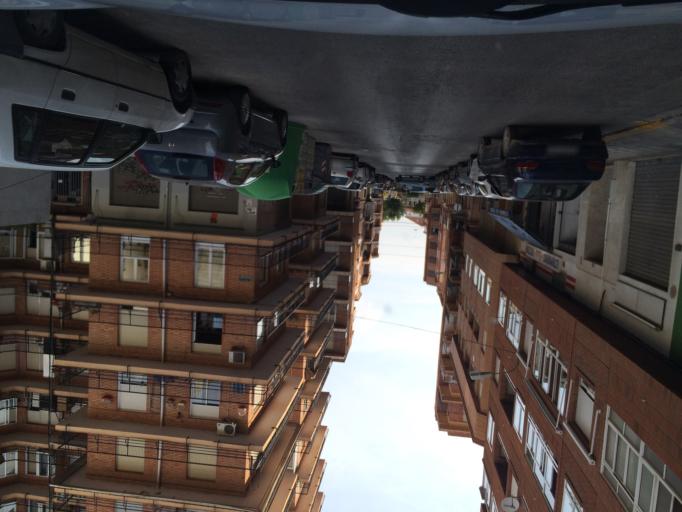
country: ES
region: Castille-La Mancha
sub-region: Provincia de Albacete
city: Albacete
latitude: 38.9898
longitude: -1.8671
